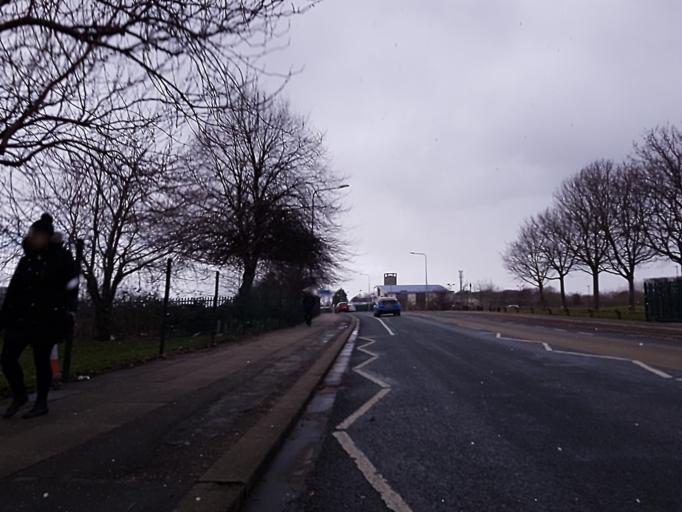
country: GB
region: England
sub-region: North East Lincolnshire
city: Grimbsy
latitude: 53.5568
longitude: -0.1022
